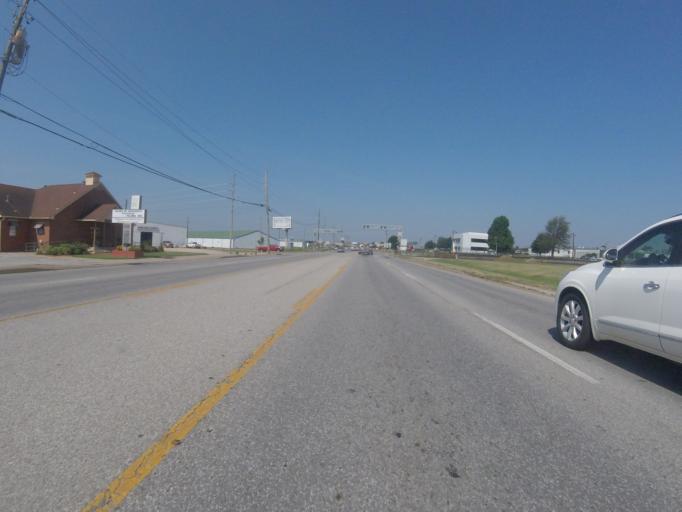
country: US
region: Arkansas
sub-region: Washington County
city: Springdale
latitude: 36.1673
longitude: -94.1355
